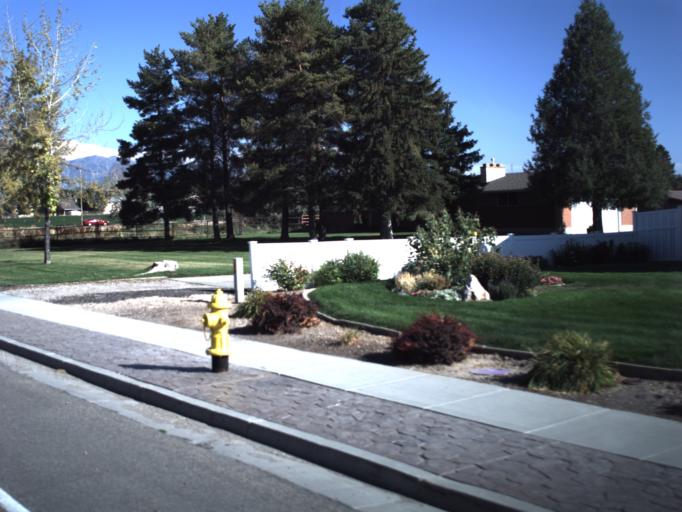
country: US
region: Utah
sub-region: Davis County
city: West Point
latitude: 41.1398
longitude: -112.0856
